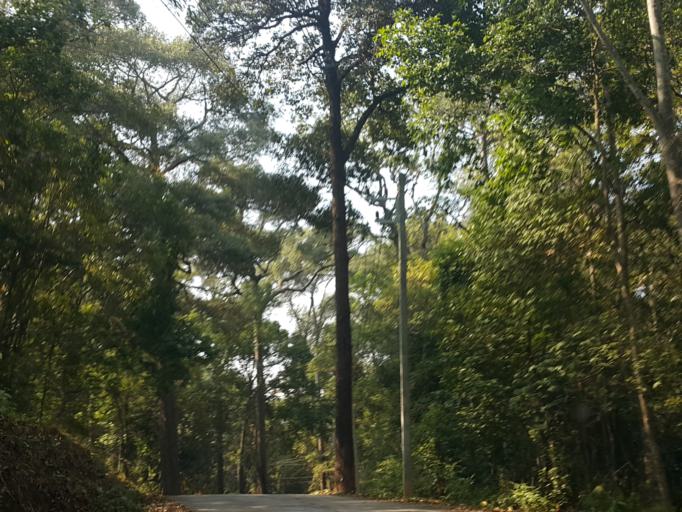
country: TH
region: Chiang Mai
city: Mae Taeng
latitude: 19.0227
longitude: 98.7940
